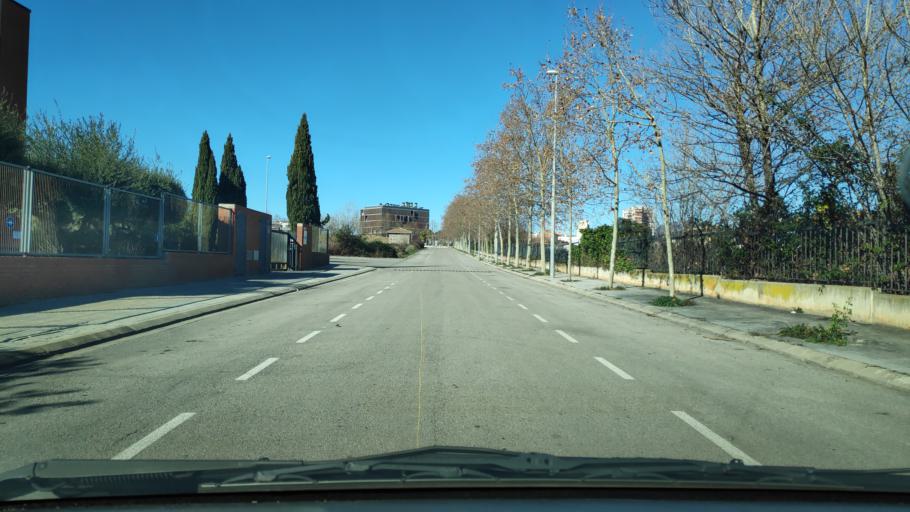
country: ES
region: Catalonia
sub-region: Provincia de Barcelona
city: Sant Quirze del Valles
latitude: 41.5383
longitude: 2.0924
